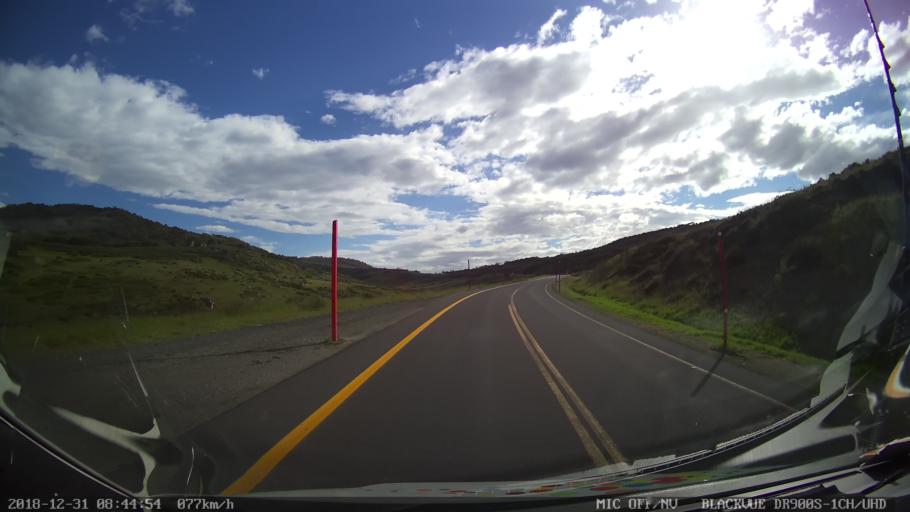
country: AU
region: New South Wales
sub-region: Snowy River
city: Jindabyne
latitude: -36.3799
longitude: 148.4591
